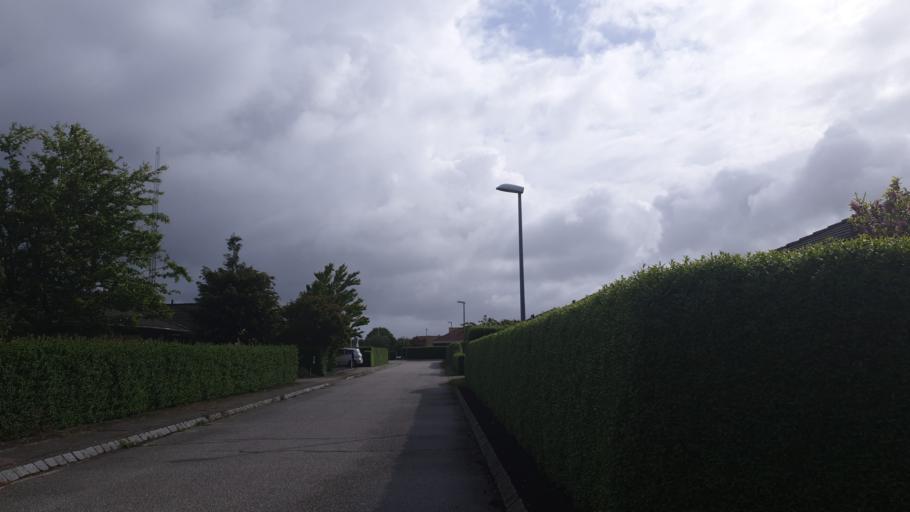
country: DK
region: Central Jutland
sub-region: Hedensted Kommune
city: Hedensted
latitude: 55.7927
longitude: 9.6920
